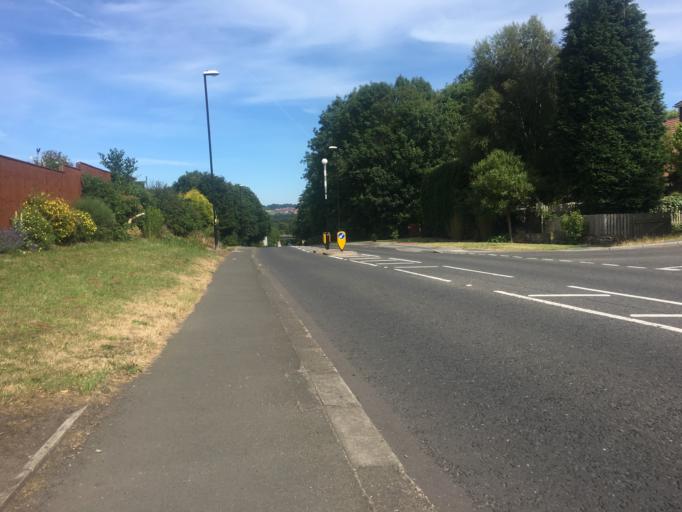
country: GB
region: England
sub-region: Sunderland
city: Washington
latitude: 54.8793
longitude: -1.5317
